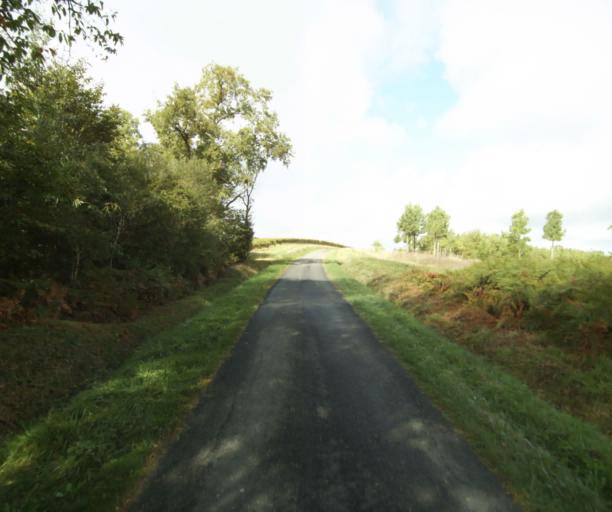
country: FR
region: Midi-Pyrenees
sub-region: Departement du Gers
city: Cazaubon
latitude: 43.8459
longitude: -0.0756
